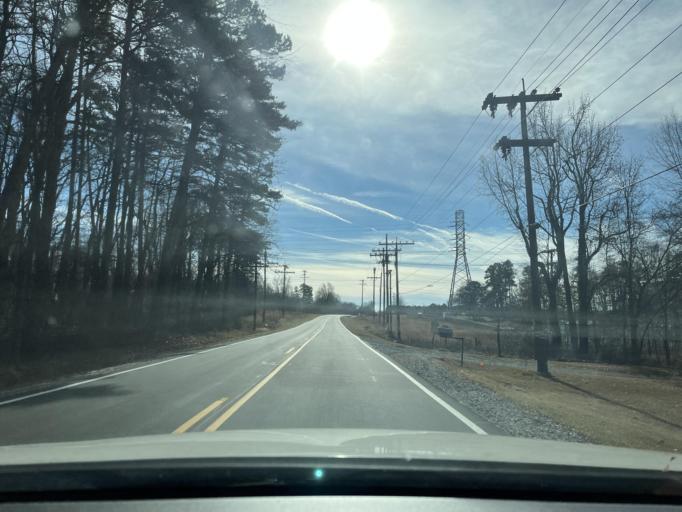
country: US
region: North Carolina
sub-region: Guilford County
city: Pleasant Garden
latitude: 36.0116
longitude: -79.7778
